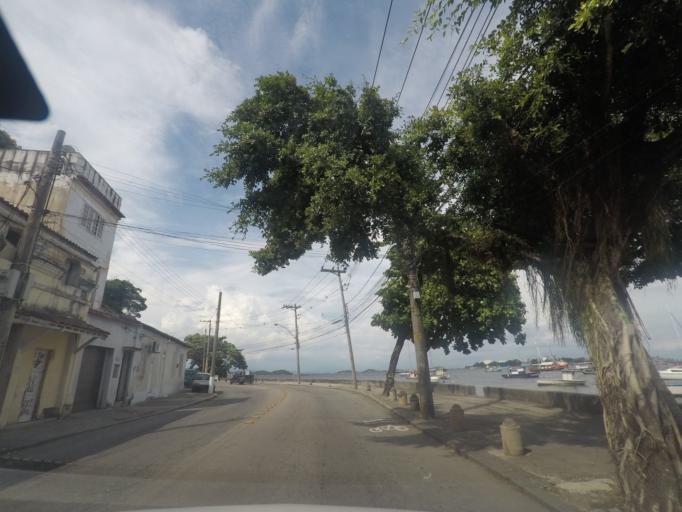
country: BR
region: Rio de Janeiro
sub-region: Rio De Janeiro
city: Rio de Janeiro
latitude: -22.8189
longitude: -43.1753
